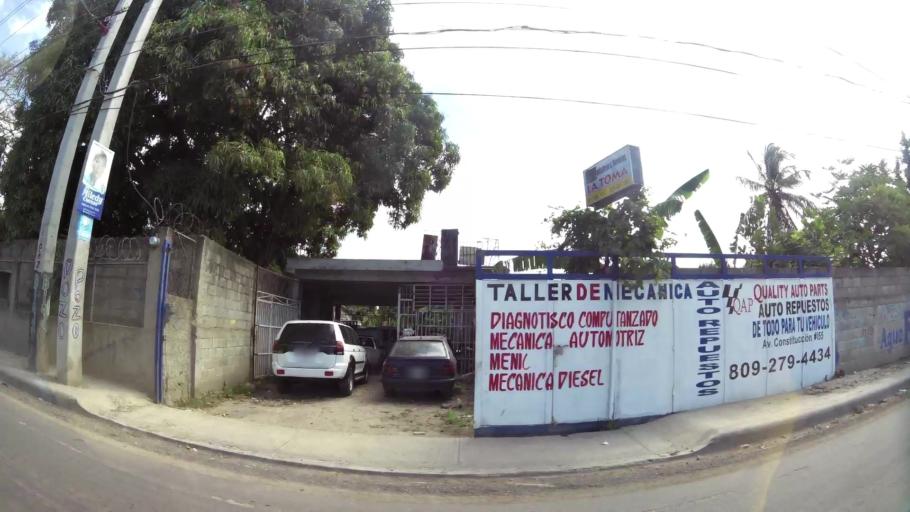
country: DO
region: San Cristobal
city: San Cristobal
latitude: 18.4322
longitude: -70.1261
